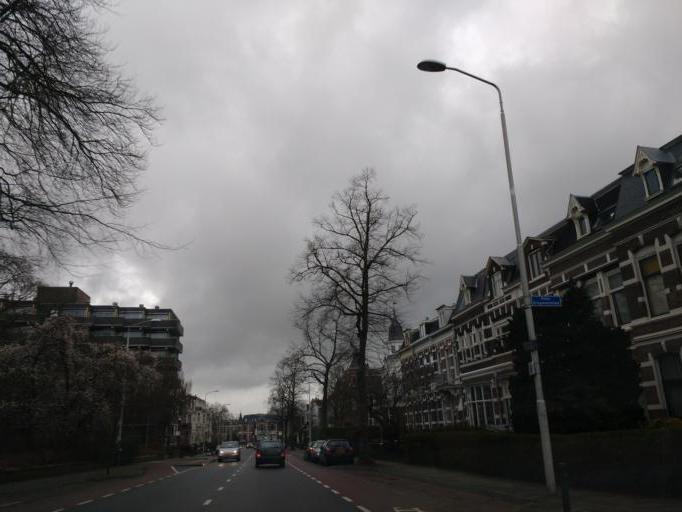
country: NL
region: Gelderland
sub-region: Gemeente Nijmegen
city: Nijmegen
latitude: 51.8414
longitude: 5.8765
